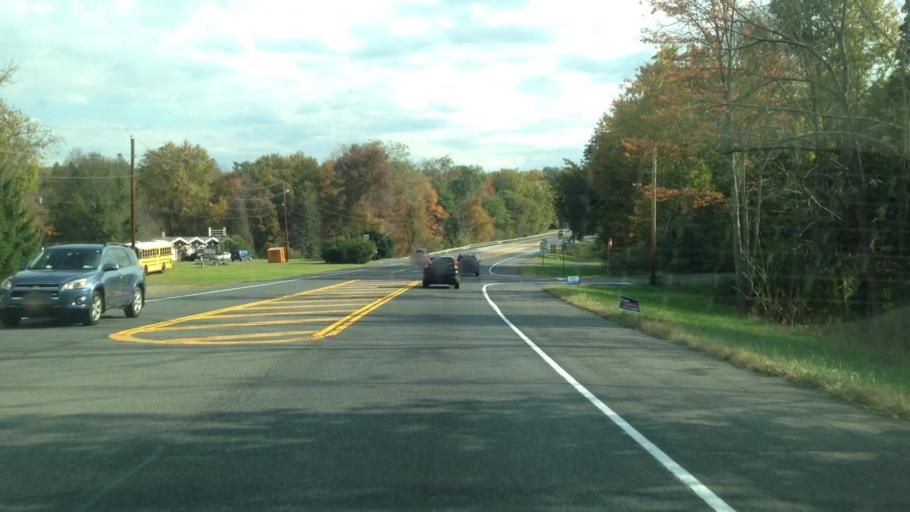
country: US
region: New York
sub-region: Ulster County
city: Highland
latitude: 41.7447
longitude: -73.9875
